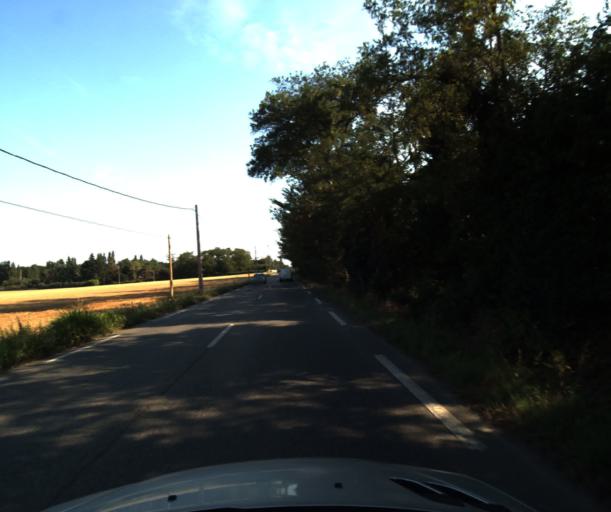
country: FR
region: Midi-Pyrenees
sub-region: Departement de la Haute-Garonne
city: Labarthe-sur-Leze
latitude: 43.4711
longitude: 1.3979
